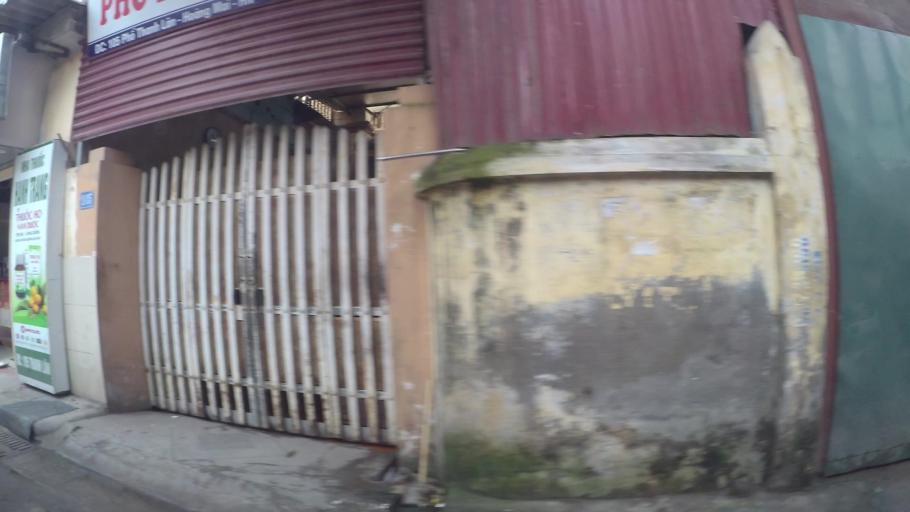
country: VN
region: Ha Noi
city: Hai BaTrung
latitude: 20.9897
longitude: 105.8886
